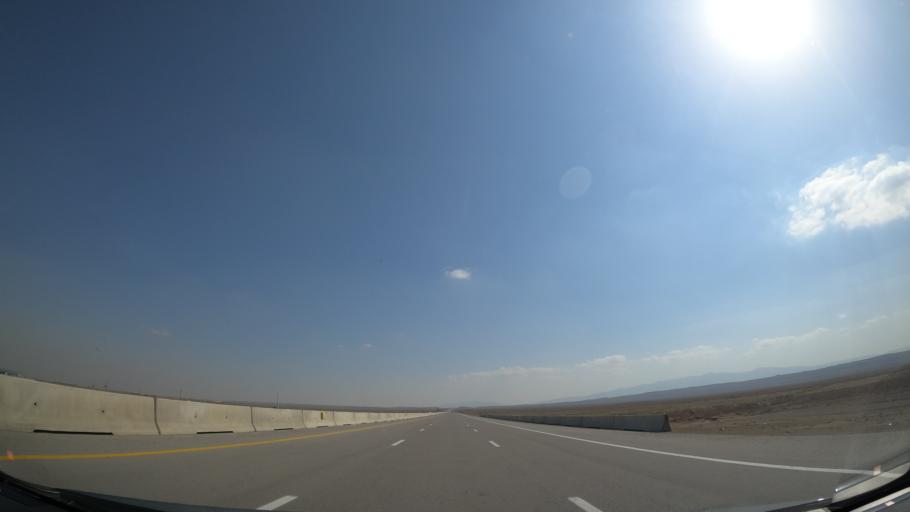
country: IR
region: Alborz
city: Nazarabad
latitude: 35.8331
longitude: 50.4971
